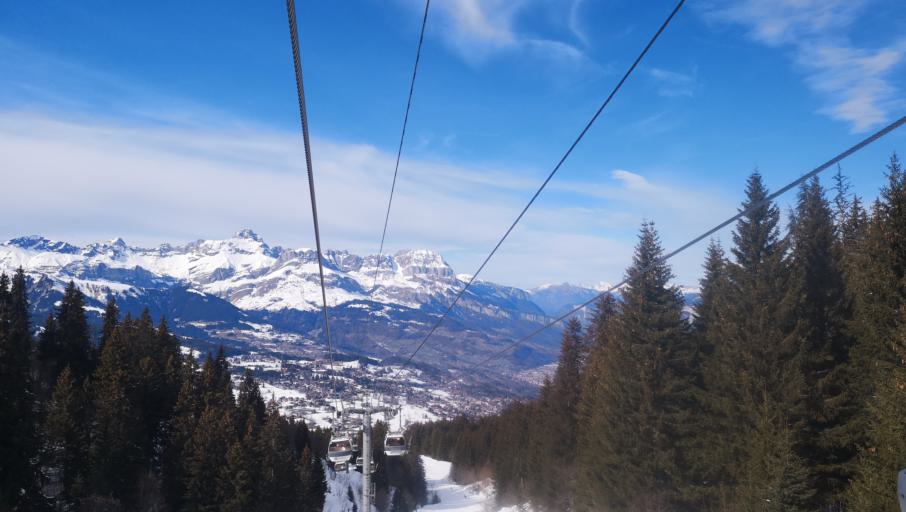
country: FR
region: Rhone-Alpes
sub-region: Departement de la Haute-Savoie
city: Combloux
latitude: 45.8621
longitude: 6.6594
